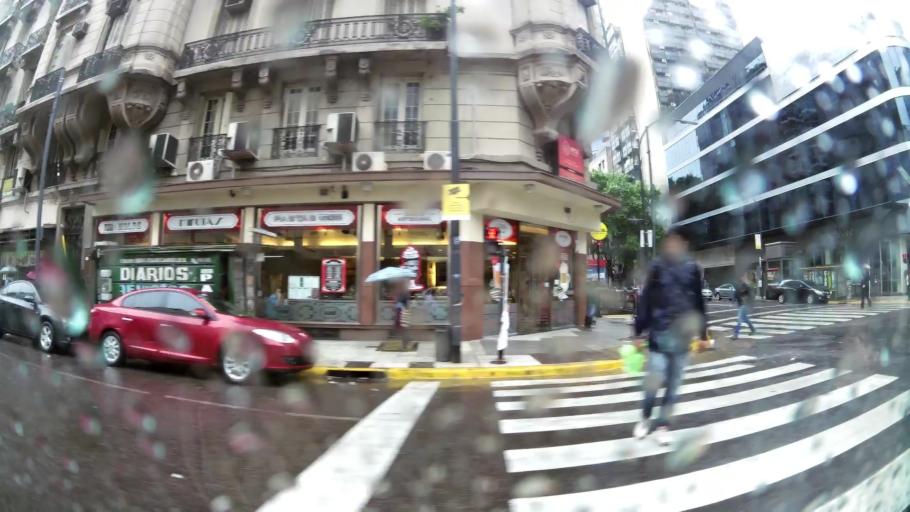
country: AR
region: Buenos Aires F.D.
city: Buenos Aires
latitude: -34.6045
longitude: -58.3924
